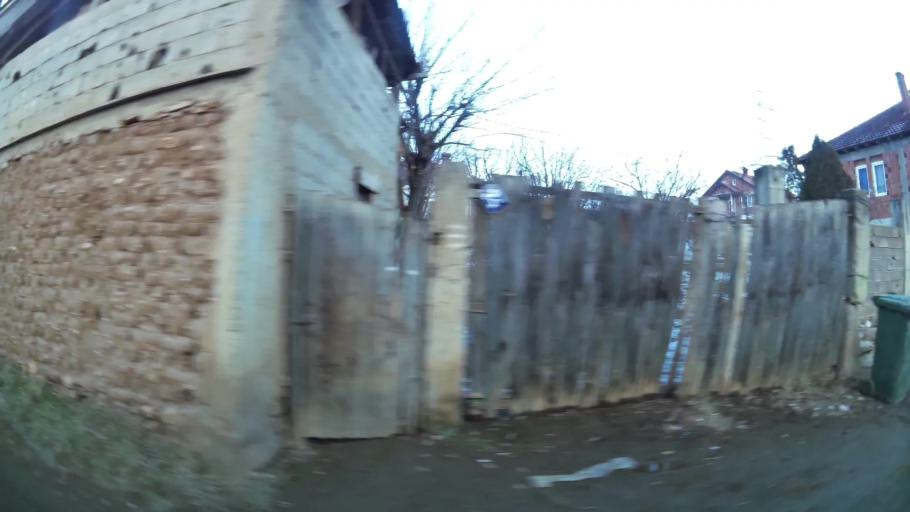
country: MK
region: Aracinovo
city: Arachinovo
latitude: 42.0291
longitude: 21.5599
